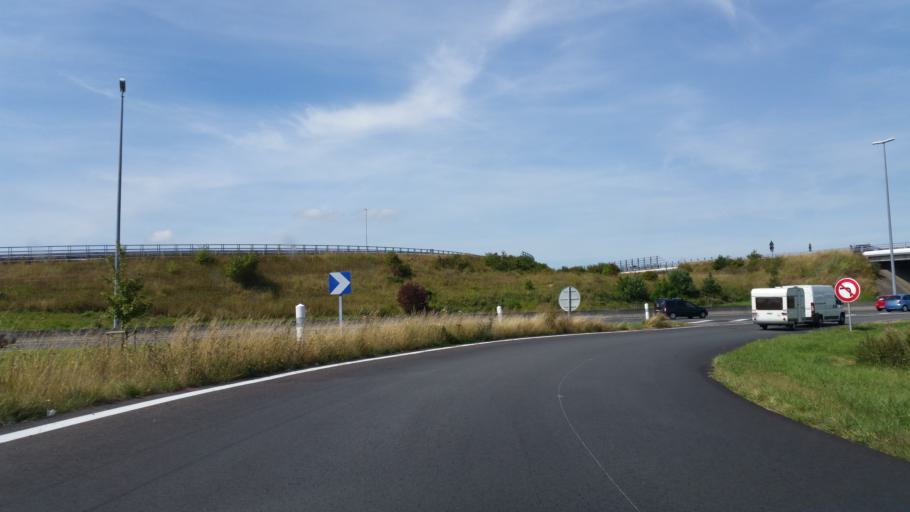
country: FR
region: Picardie
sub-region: Departement de la Somme
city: Chaulnes
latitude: 49.8514
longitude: 2.8332
